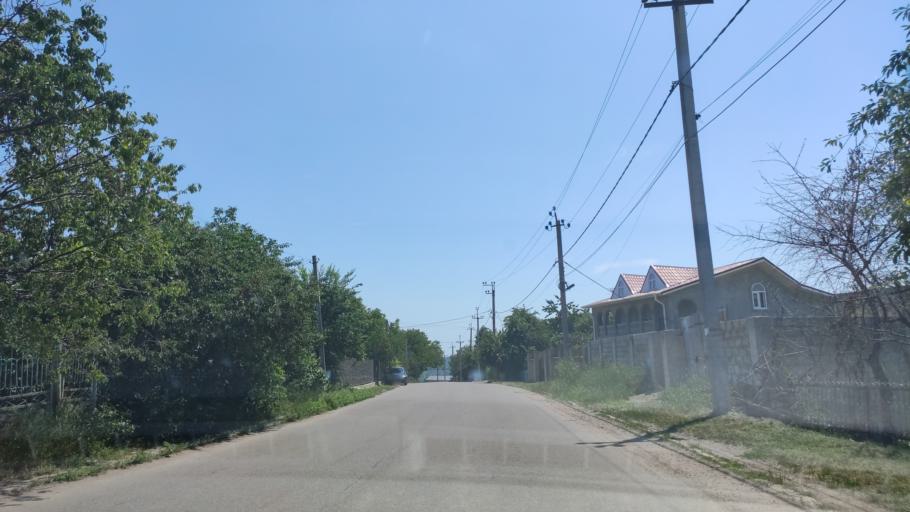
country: MD
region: Raionul Soroca
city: Soroca
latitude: 48.1499
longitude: 28.2785
